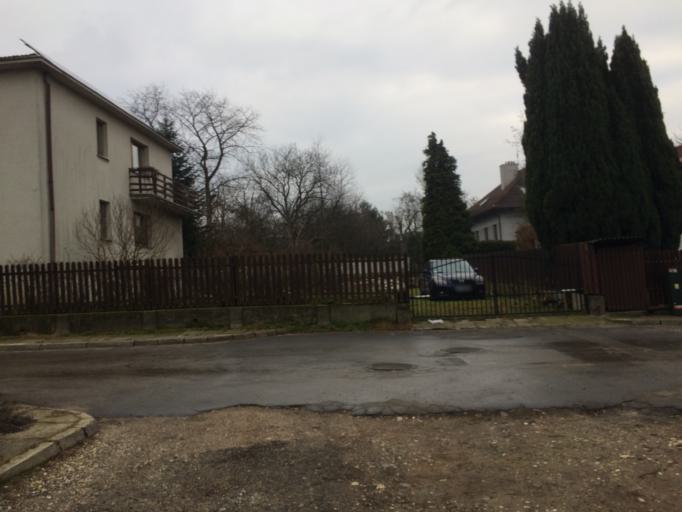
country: PL
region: Lesser Poland Voivodeship
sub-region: Powiat wielicki
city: Czarnochowice
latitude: 50.0120
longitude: 20.0304
